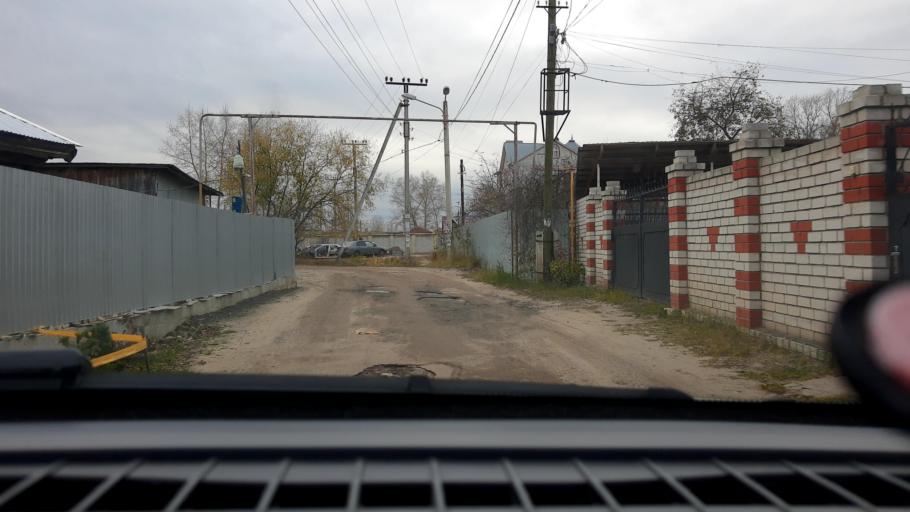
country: RU
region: Nizjnij Novgorod
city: Gorbatovka
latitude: 56.3778
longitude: 43.8022
